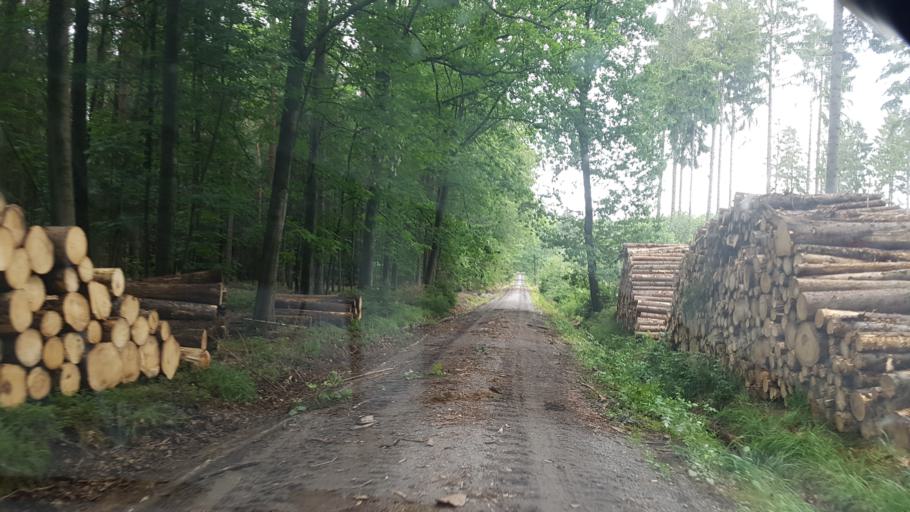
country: DE
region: Saxony
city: Grossrohrsdorf
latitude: 51.1621
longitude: 14.0301
